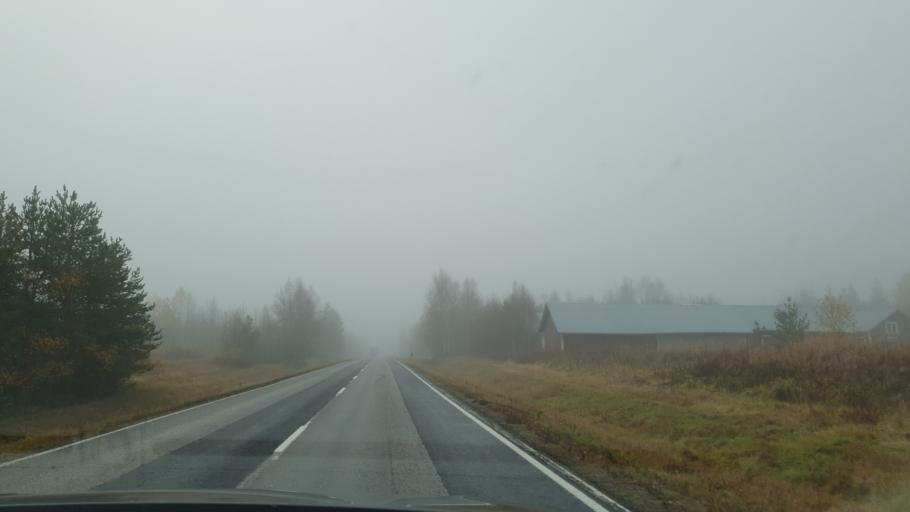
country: FI
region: Lapland
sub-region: Tunturi-Lappi
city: Kittilae
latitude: 67.2022
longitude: 24.9324
